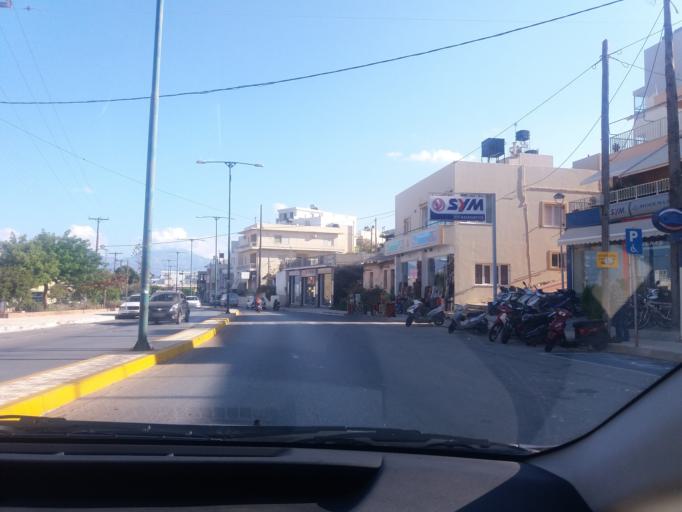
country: GR
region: Crete
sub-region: Nomos Lasithiou
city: Agios Nikolaos
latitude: 35.1968
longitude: 25.7112
